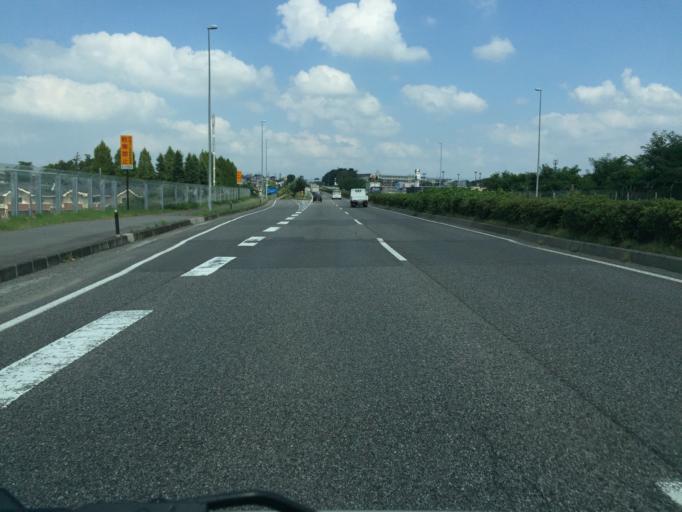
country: JP
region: Fukushima
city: Koriyama
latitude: 37.4183
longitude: 140.3527
